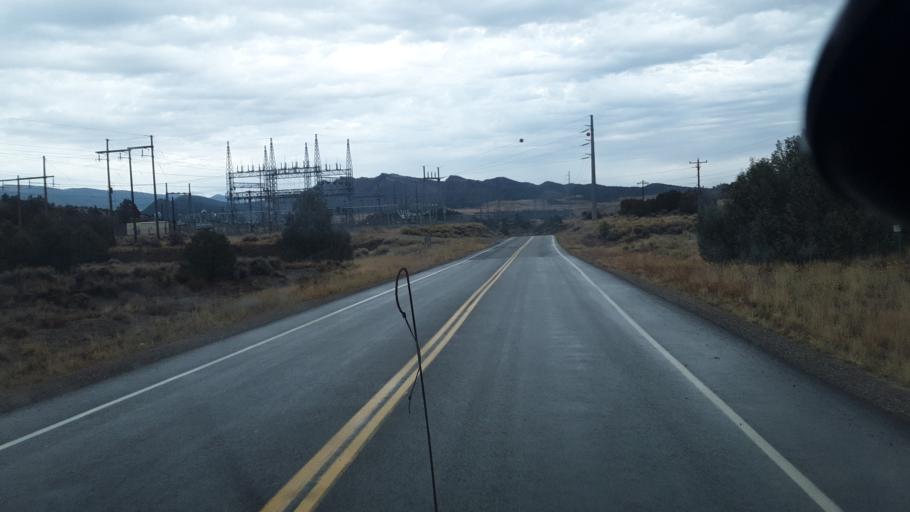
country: US
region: Colorado
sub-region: La Plata County
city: Durango
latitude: 37.2424
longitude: -107.9010
